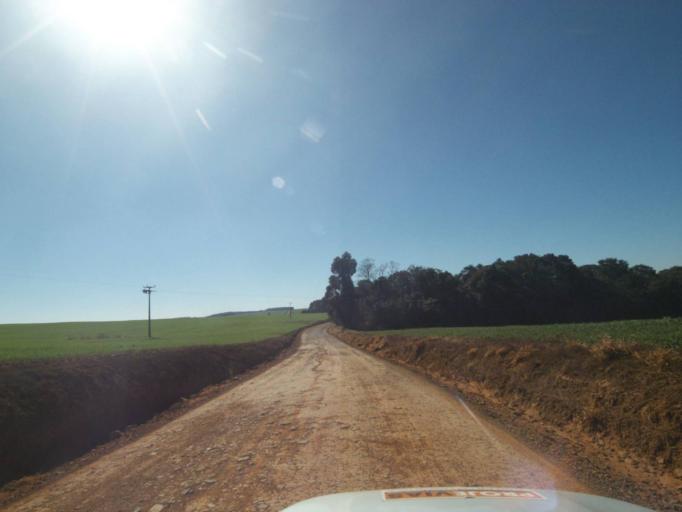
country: BR
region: Parana
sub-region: Tibagi
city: Tibagi
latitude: -24.6174
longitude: -50.6075
